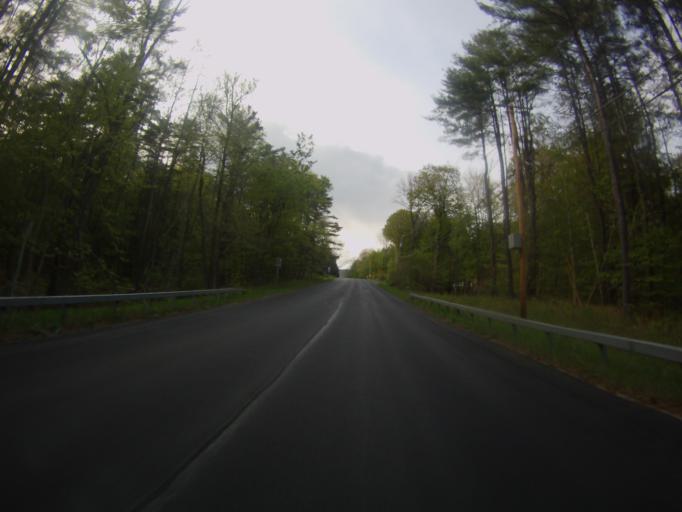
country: US
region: New York
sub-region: Essex County
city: Ticonderoga
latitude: 43.7987
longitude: -73.4865
